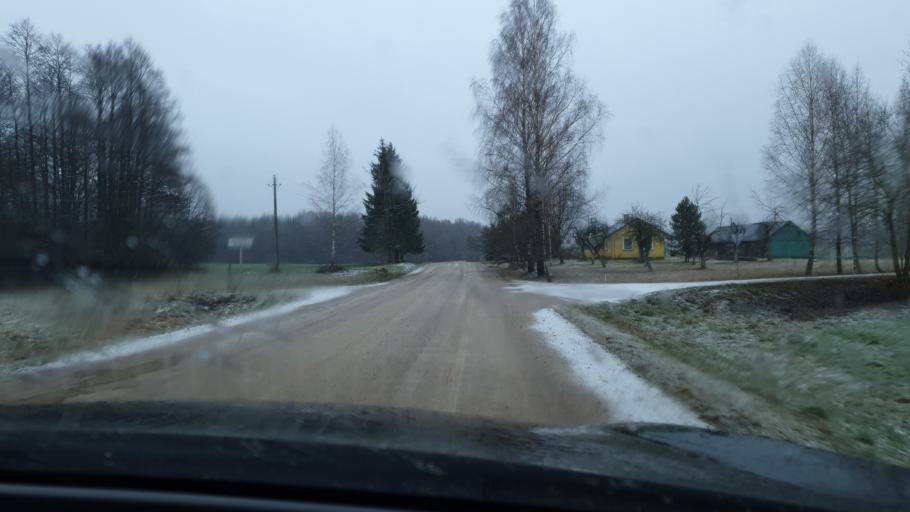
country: LT
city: Jieznas
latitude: 54.5710
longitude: 24.3179
